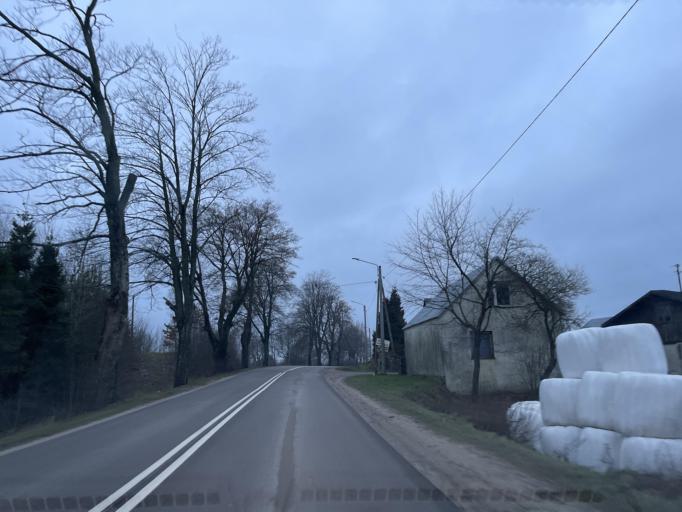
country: PL
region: Pomeranian Voivodeship
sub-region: Powiat kartuski
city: Przodkowo
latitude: 54.4018
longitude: 18.2210
